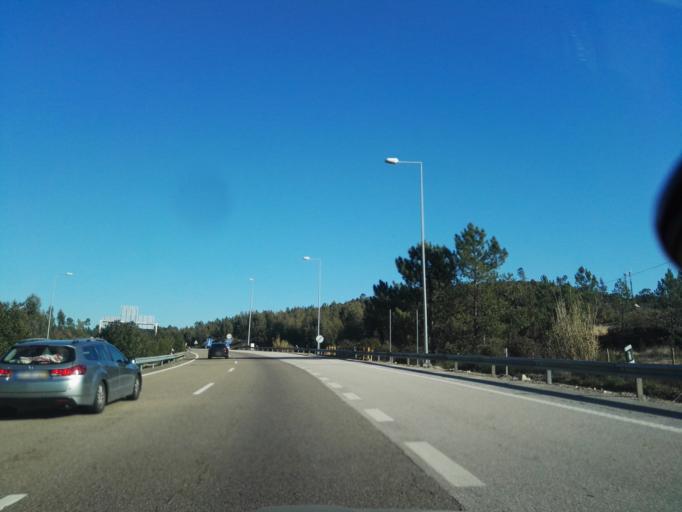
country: PT
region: Santarem
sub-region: Entroncamento
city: Entroncamento
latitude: 39.4886
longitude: -8.4446
